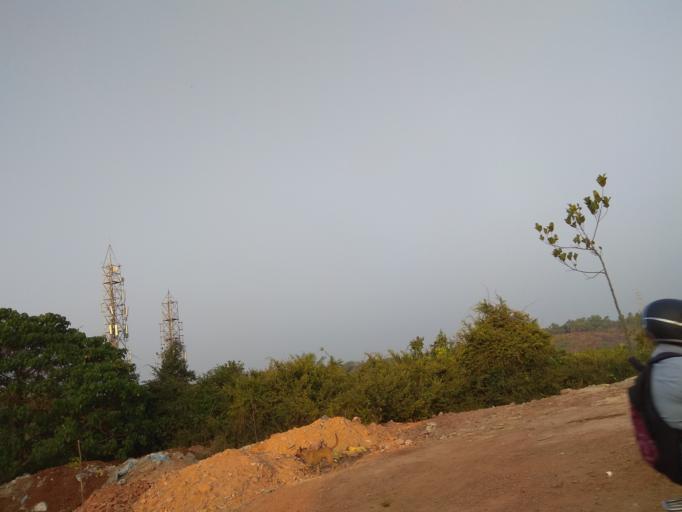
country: IN
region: Karnataka
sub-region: Dakshina Kannada
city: Mangalore
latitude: 12.9173
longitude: 74.8591
